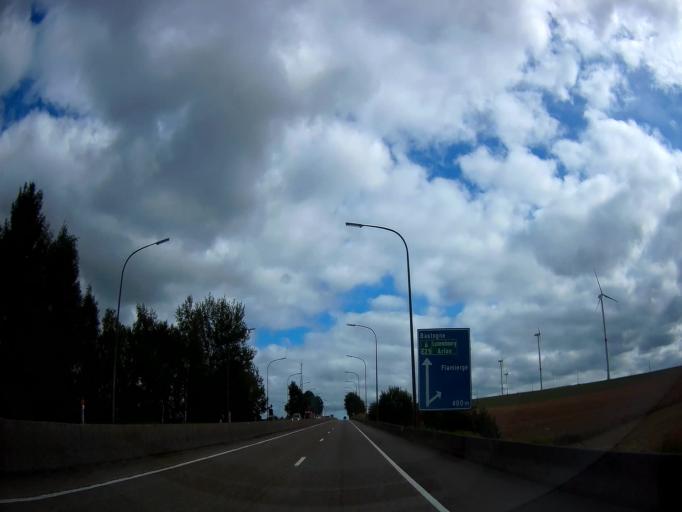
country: BE
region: Wallonia
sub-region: Province du Luxembourg
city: Sainte-Ode
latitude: 50.0329
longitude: 5.5907
